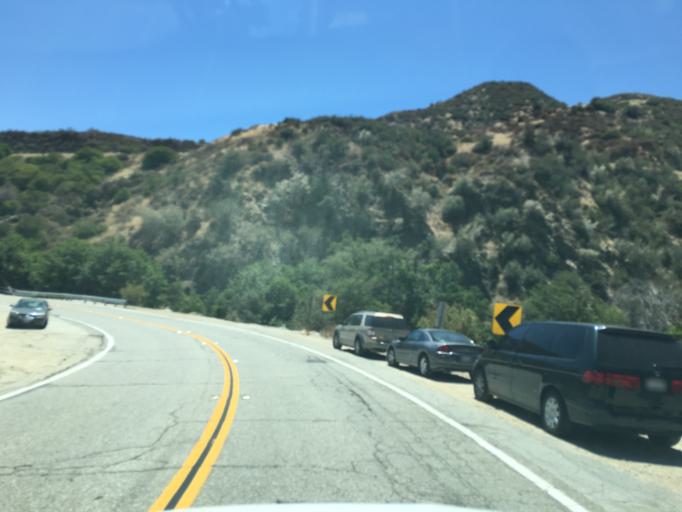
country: US
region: California
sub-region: San Bernardino County
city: San Antonio Heights
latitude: 34.1783
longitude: -117.6750
